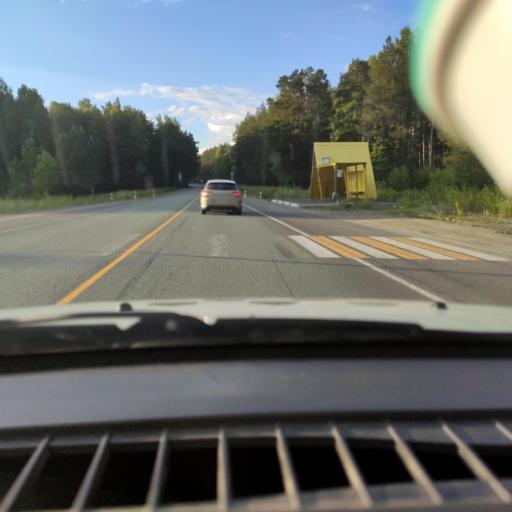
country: RU
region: Chelyabinsk
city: Turgoyak
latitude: 55.2669
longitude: 60.1975
